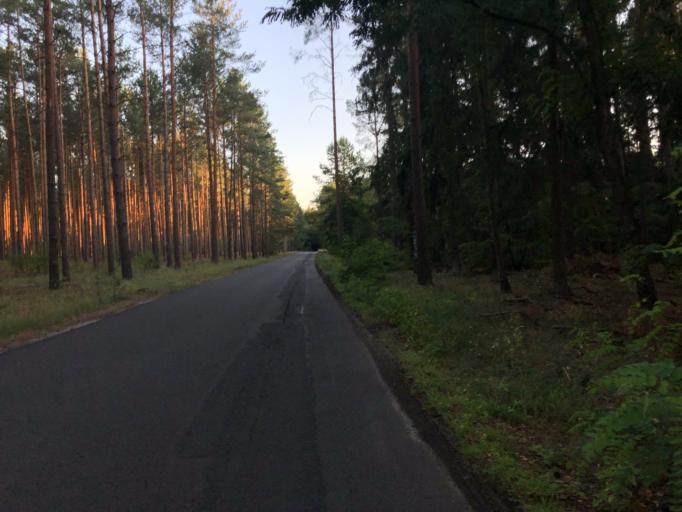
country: DE
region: Brandenburg
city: Gross Lindow
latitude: 52.2528
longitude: 14.4784
